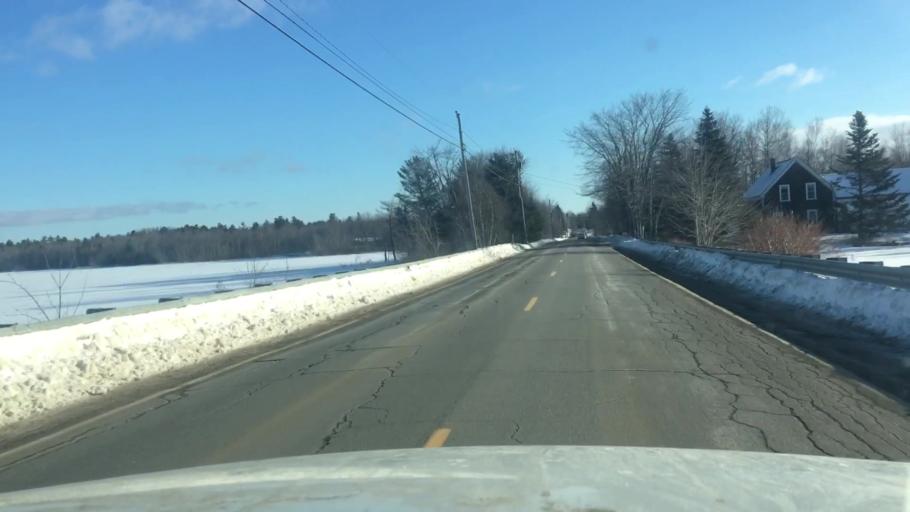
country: US
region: Maine
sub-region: Hancock County
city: Ellsworth
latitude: 44.5918
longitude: -68.4142
